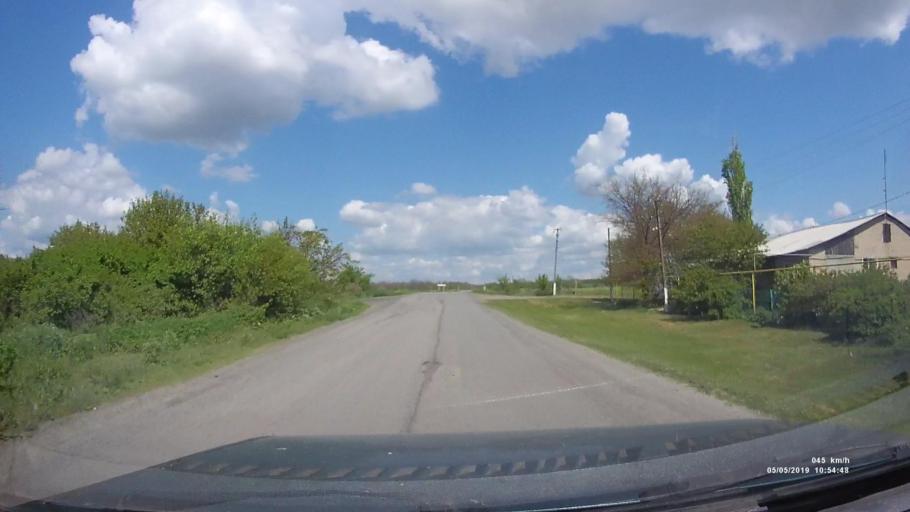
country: RU
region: Rostov
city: Ust'-Donetskiy
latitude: 47.6607
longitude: 40.8224
